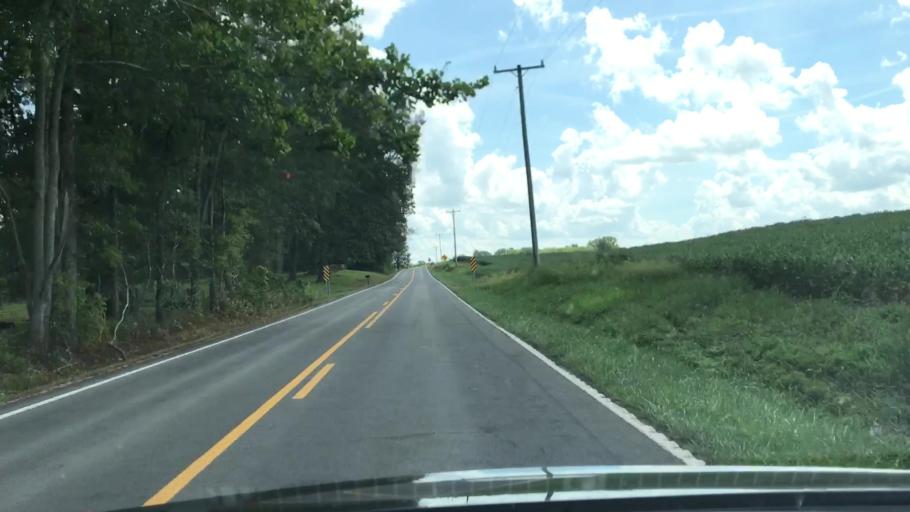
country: US
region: Tennessee
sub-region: Robertson County
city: Springfield
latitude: 36.5726
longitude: -86.8650
